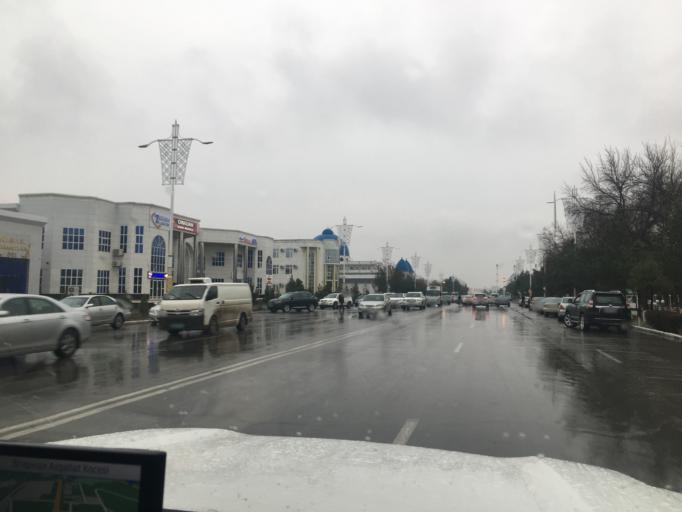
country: TM
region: Mary
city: Mary
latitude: 37.5928
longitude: 61.8420
